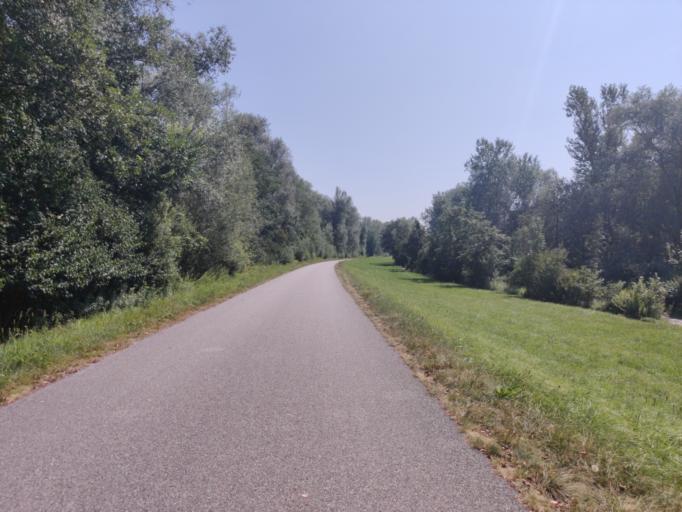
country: AT
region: Upper Austria
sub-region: Politischer Bezirk Urfahr-Umgebung
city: Feldkirchen an der Donau
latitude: 48.3240
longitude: 14.0513
